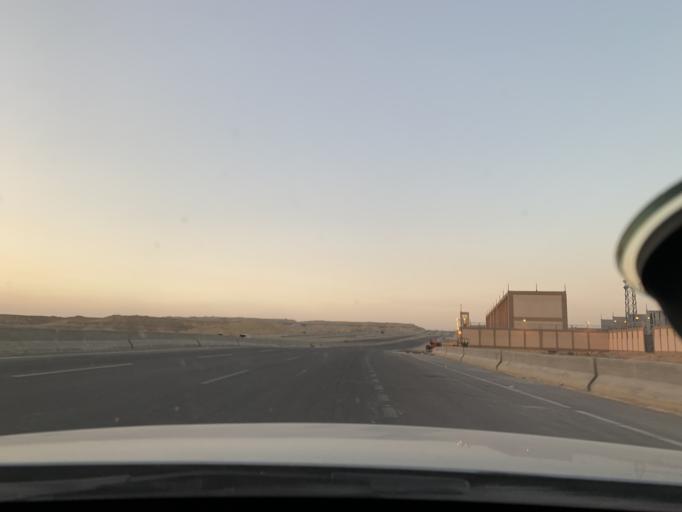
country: EG
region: Muhafazat al Qahirah
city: Halwan
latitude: 29.9371
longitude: 31.5292
